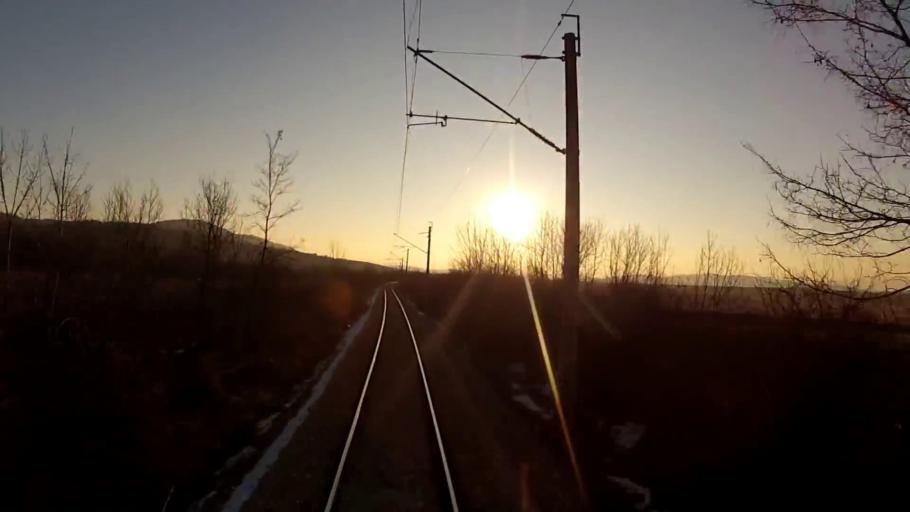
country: BG
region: Sofiya
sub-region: Obshtina Dragoman
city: Dragoman
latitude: 42.8957
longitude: 22.9661
